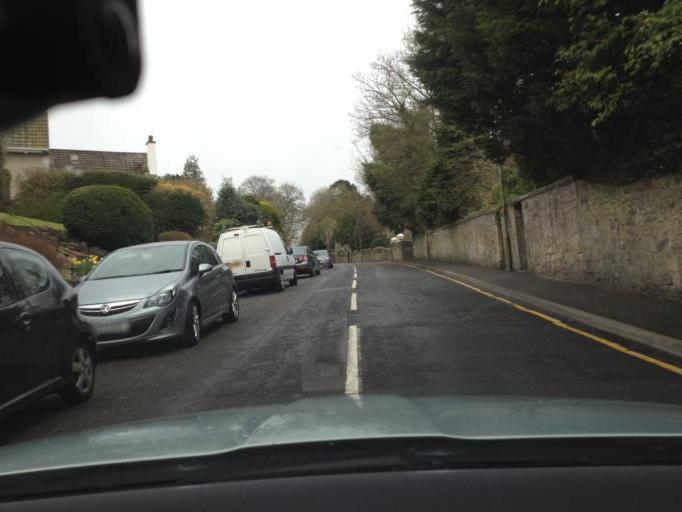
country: GB
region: Scotland
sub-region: West Lothian
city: Linlithgow
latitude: 55.9743
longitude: -3.5971
